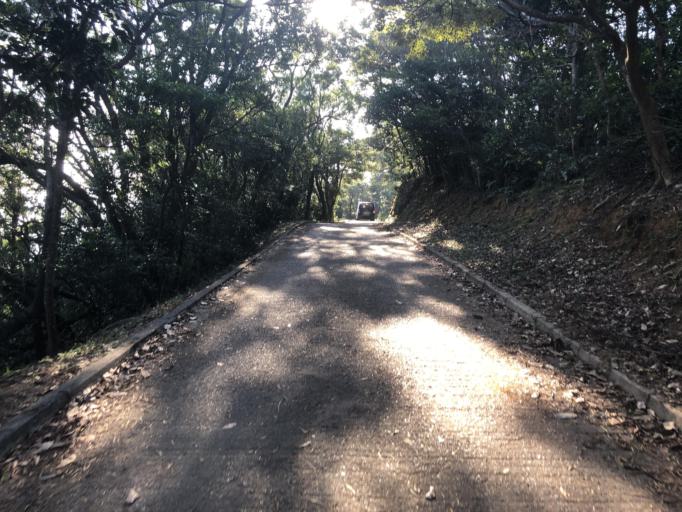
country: HK
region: Tsuen Wan
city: Tsuen Wan
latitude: 22.3973
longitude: 114.0800
